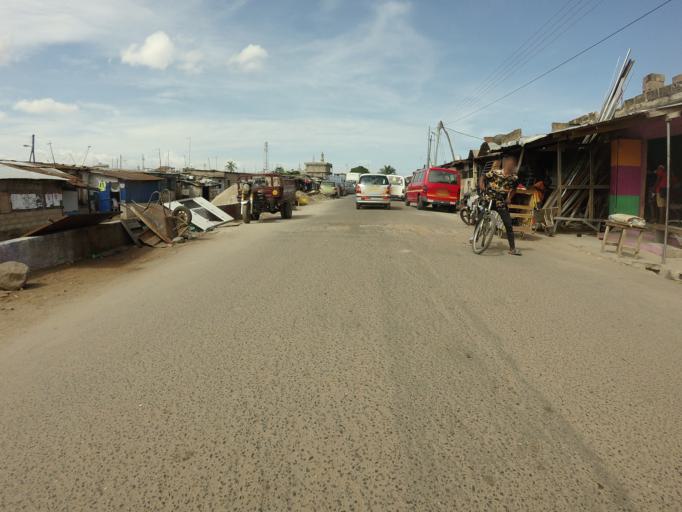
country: GH
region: Greater Accra
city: Accra
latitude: 5.5881
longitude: -0.1982
